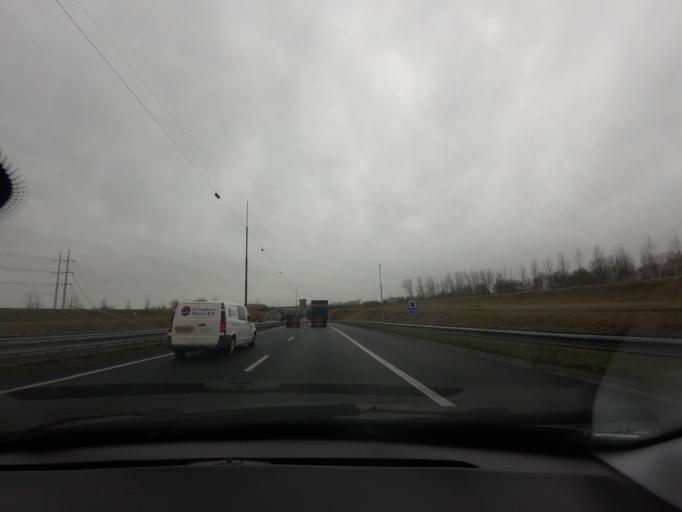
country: NL
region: North Holland
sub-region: Gemeente Velsen
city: Velsen-Zuid
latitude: 52.4627
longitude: 4.6730
